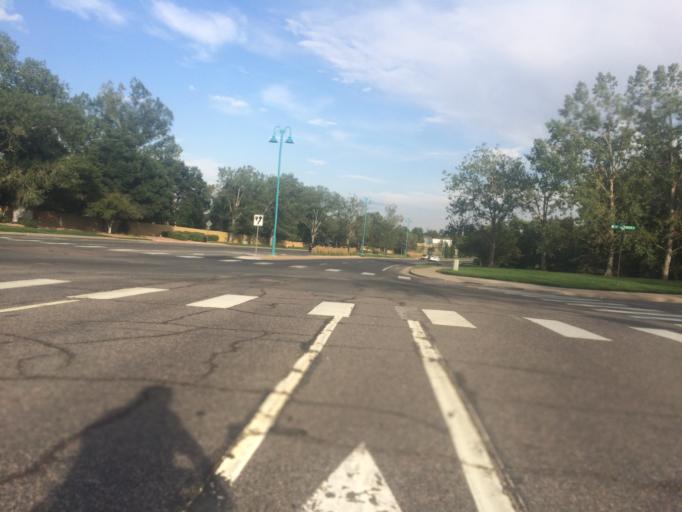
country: US
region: Colorado
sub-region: Boulder County
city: Superior
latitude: 39.9387
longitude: -105.1511
